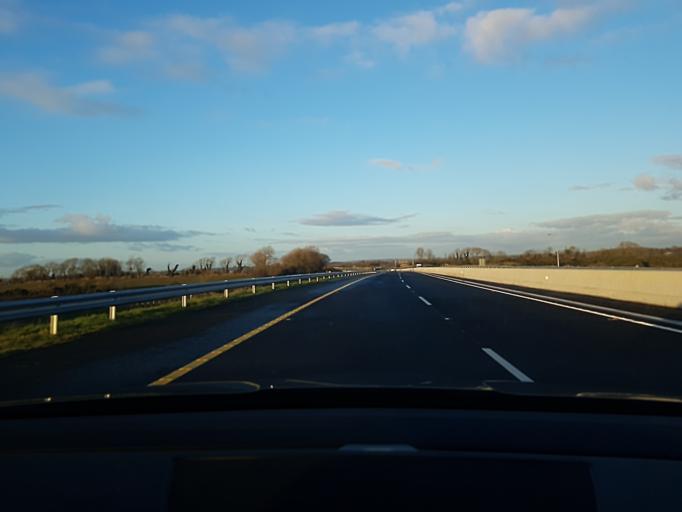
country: IE
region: Connaught
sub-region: County Galway
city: Athenry
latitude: 53.2990
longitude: -8.8061
